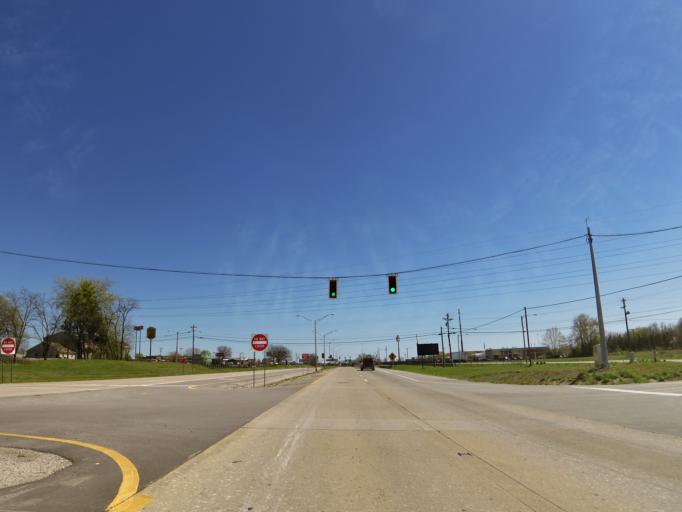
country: US
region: Kentucky
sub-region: Warren County
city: Bowling Green
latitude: 37.0092
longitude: -86.3778
